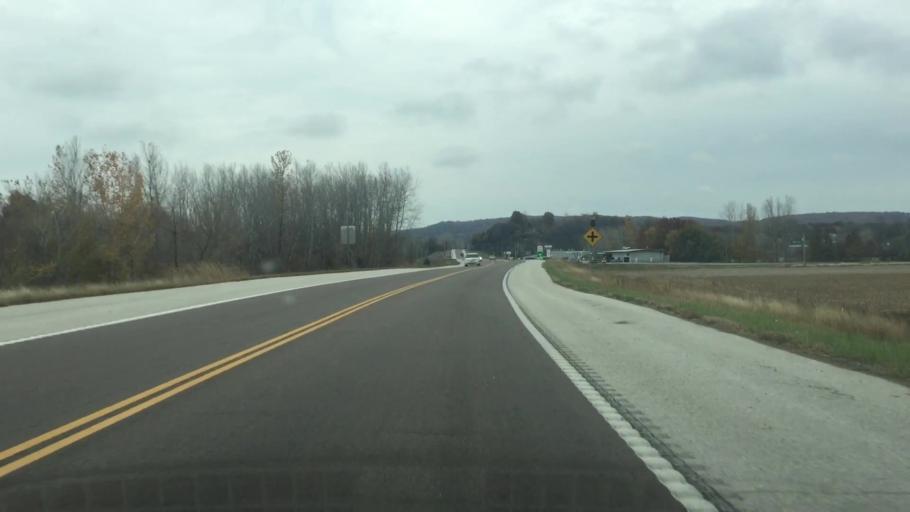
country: US
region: Missouri
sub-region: Gasconade County
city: Hermann
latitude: 38.7261
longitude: -91.4452
